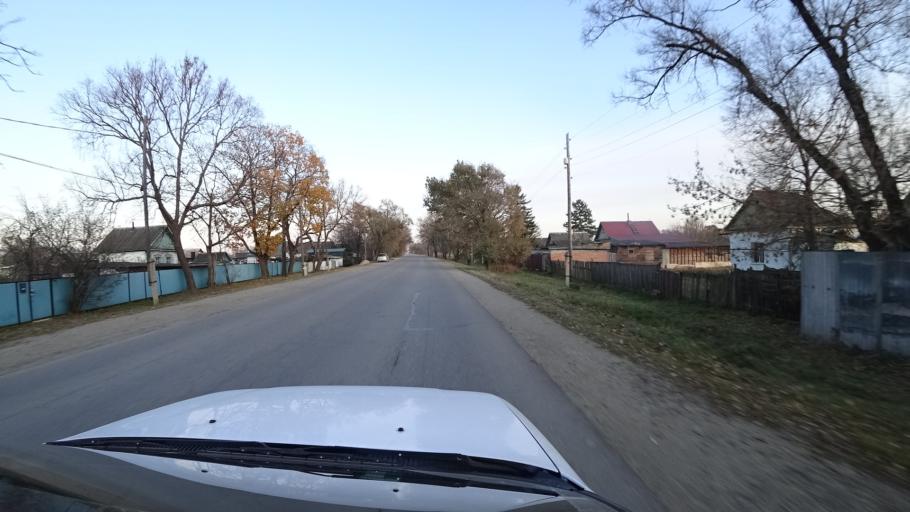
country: RU
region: Primorskiy
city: Dal'nerechensk
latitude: 45.9373
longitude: 133.8132
